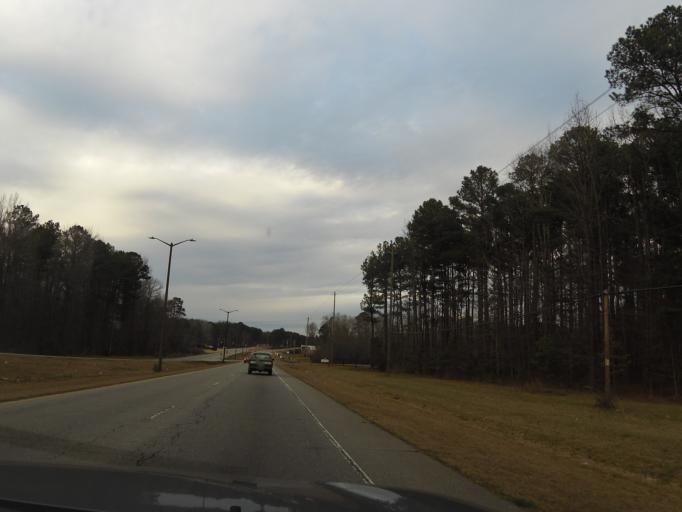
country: US
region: North Carolina
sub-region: Nash County
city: Rocky Mount
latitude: 36.0289
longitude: -77.7672
